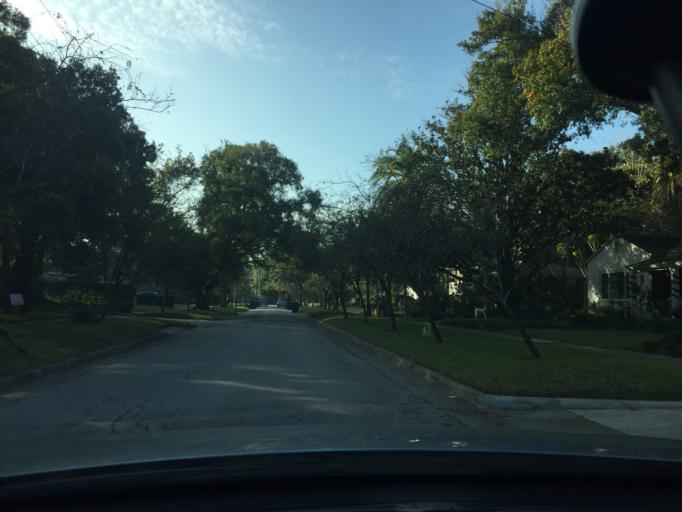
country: US
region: Florida
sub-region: Hillsborough County
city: Tampa
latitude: 27.9426
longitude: -82.4964
